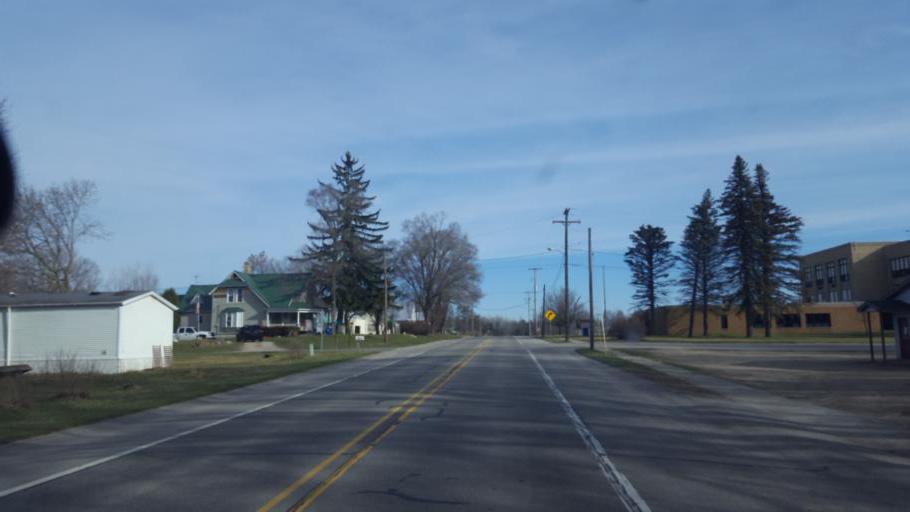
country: US
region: Michigan
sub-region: Montcalm County
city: Howard City
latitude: 43.4943
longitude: -85.4448
